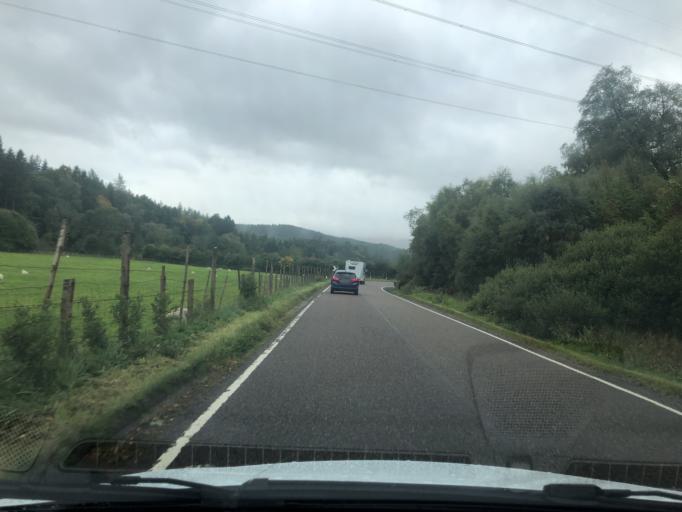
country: GB
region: Scotland
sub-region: Highland
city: Kingussie
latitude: 56.9794
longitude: -4.3755
